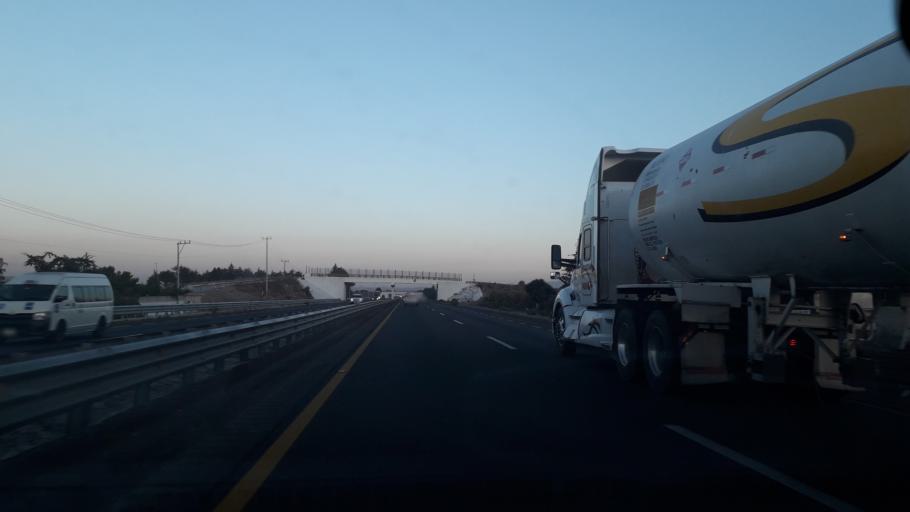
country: MX
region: Puebla
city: Palmarito Tochapan
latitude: 18.9119
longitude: -97.6363
